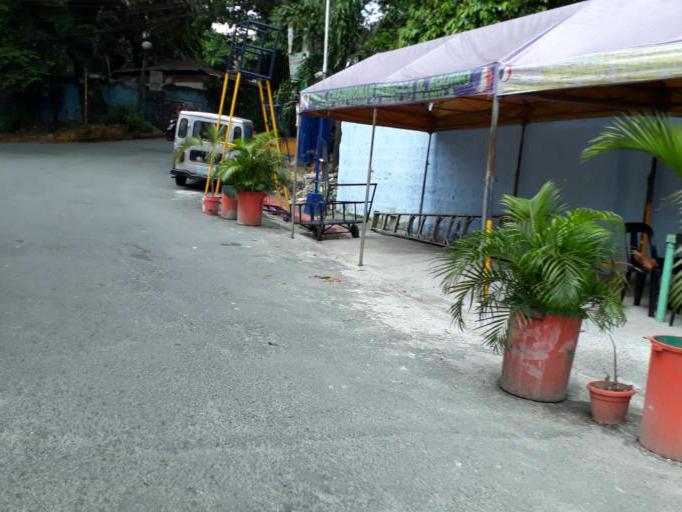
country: PH
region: Metro Manila
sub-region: City of Manila
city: Manila
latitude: 14.6103
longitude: 121.0002
